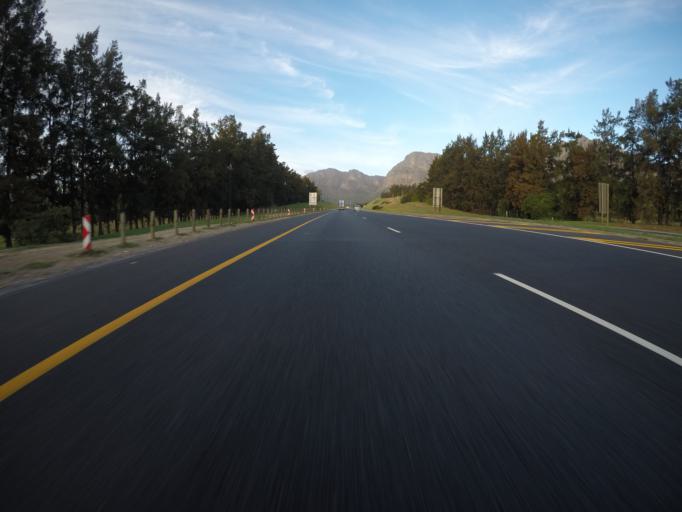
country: ZA
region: Western Cape
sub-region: Cape Winelands District Municipality
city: Paarl
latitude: -33.7436
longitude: 19.0312
